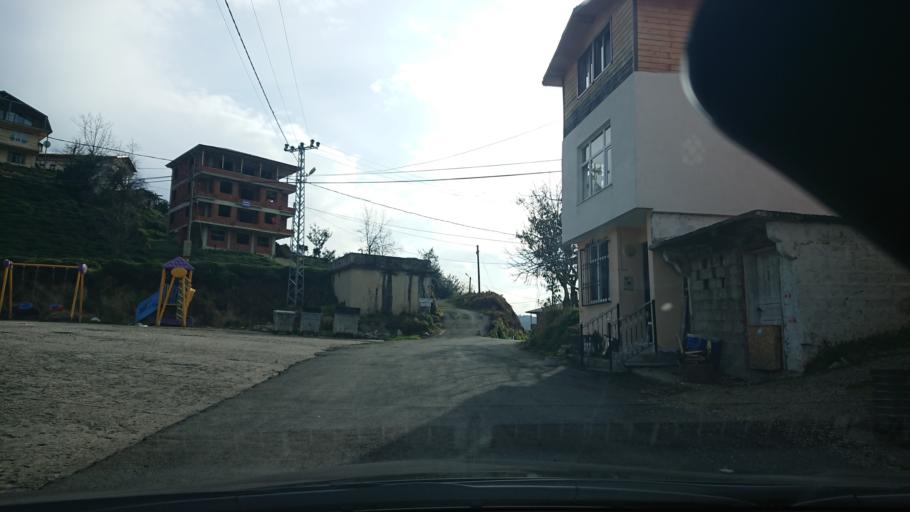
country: TR
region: Rize
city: Rize
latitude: 40.9939
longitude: 40.4928
